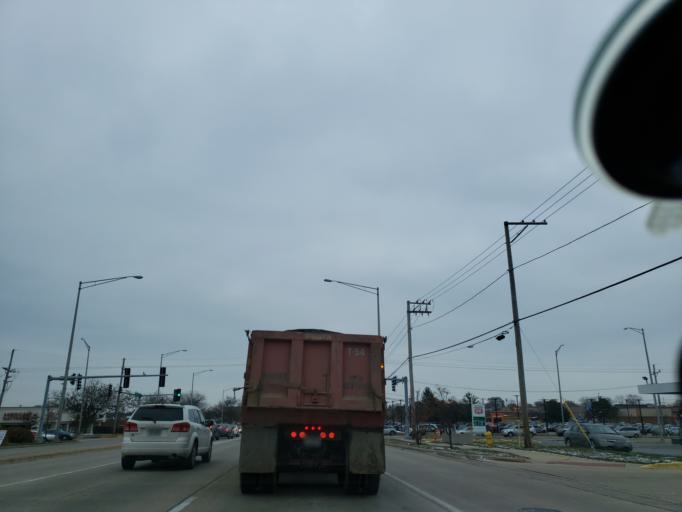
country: US
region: Illinois
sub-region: Cook County
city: Orland Hills
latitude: 41.6014
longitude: -87.8489
